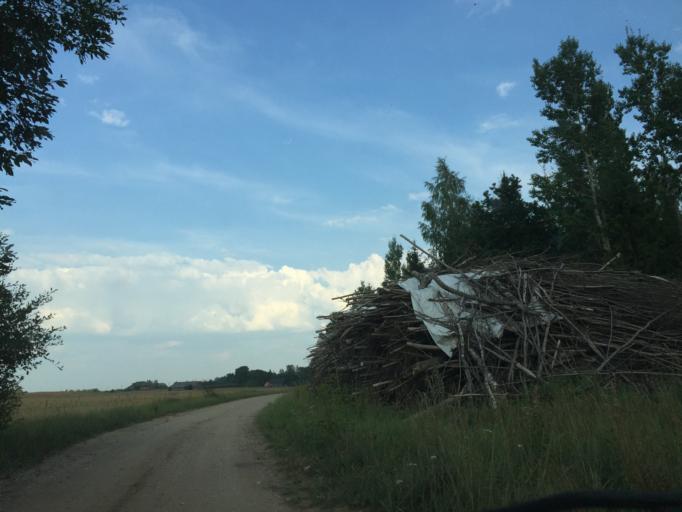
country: LT
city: Zagare
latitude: 56.4485
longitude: 23.1490
